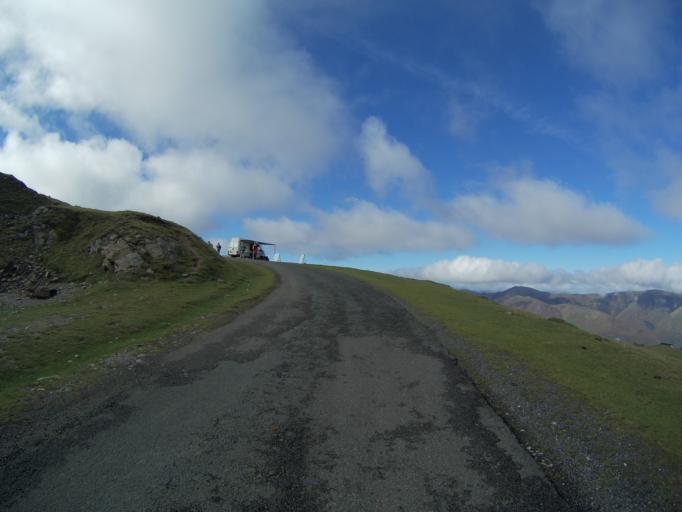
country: ES
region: Navarre
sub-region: Provincia de Navarra
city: Orbara
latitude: 43.0614
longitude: -1.2681
